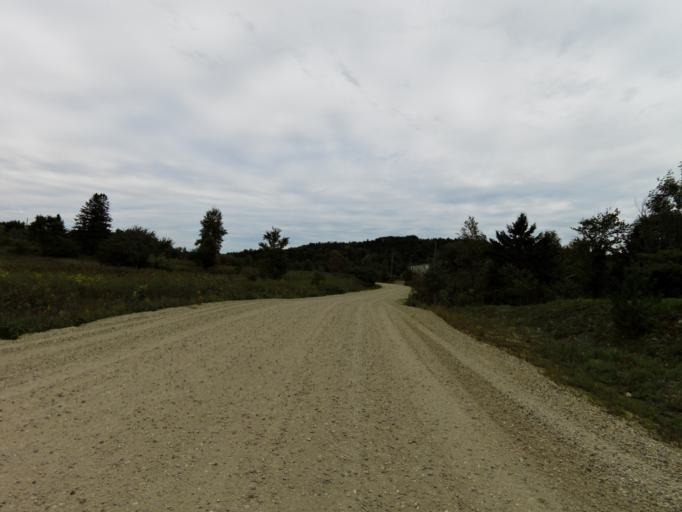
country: CA
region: Quebec
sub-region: Outaouais
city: Wakefield
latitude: 45.7734
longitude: -75.9442
